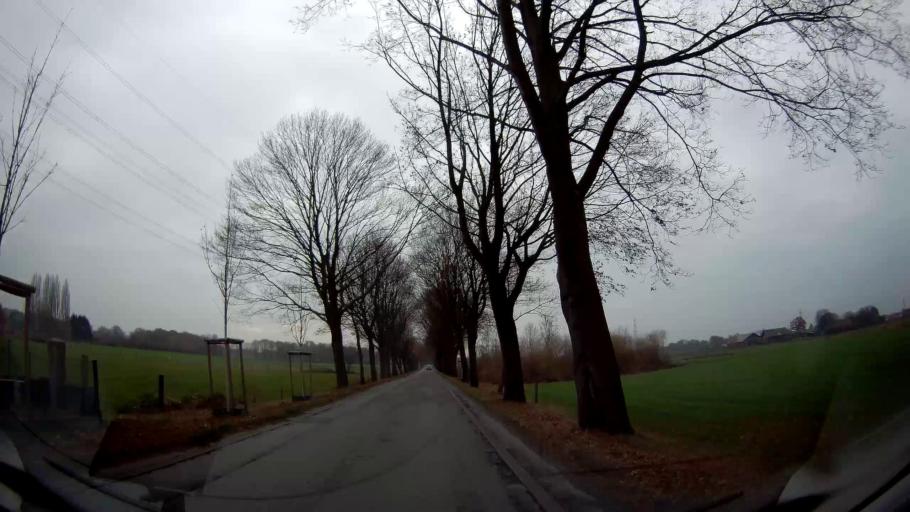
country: DE
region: North Rhine-Westphalia
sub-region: Regierungsbezirk Munster
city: Gladbeck
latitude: 51.5721
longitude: 7.0202
